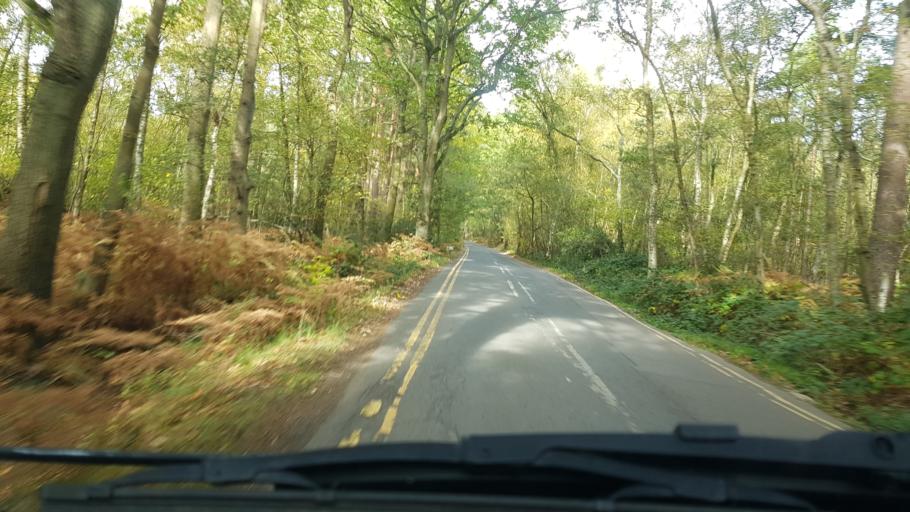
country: GB
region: England
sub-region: Surrey
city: Byfleet
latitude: 51.3165
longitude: -0.4708
